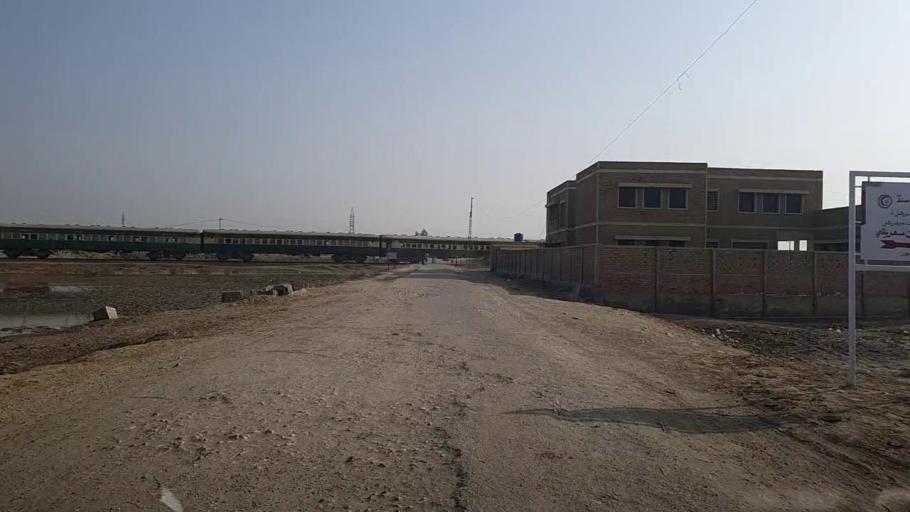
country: PK
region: Sindh
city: Kandhkot
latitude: 28.2768
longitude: 69.2548
